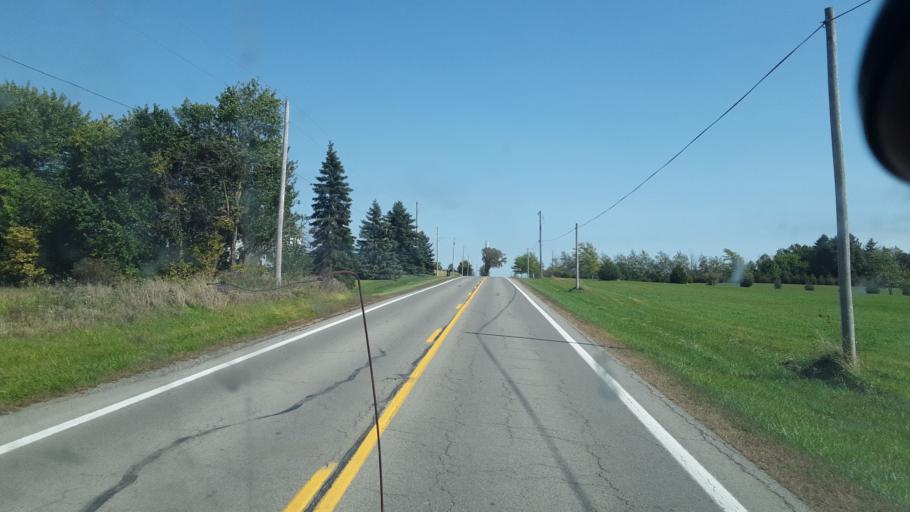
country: US
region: Ohio
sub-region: Logan County
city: Northwood
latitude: 40.5046
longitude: -83.7253
